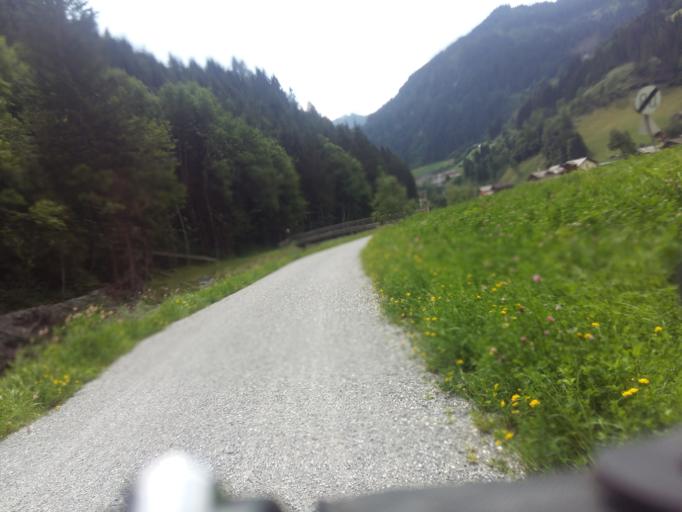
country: AT
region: Salzburg
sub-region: Politischer Bezirk Sankt Johann im Pongau
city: Schwarzach im Pongau
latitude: 47.2662
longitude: 13.2041
